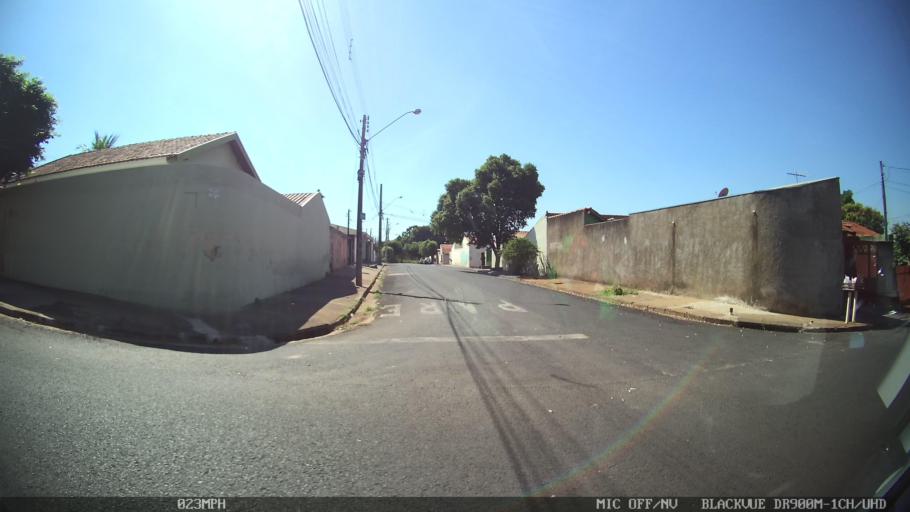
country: BR
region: Sao Paulo
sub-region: Sao Jose Do Rio Preto
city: Sao Jose do Rio Preto
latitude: -20.7754
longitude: -49.3829
